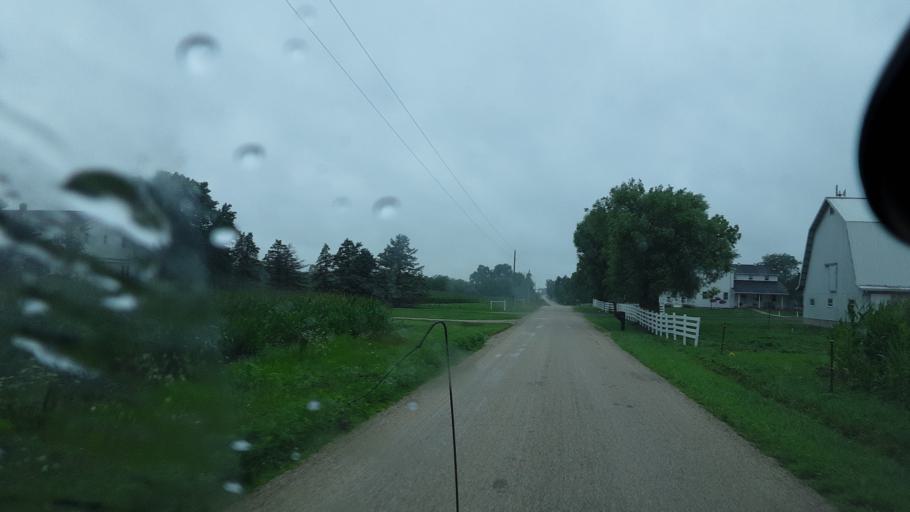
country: US
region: Indiana
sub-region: Adams County
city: Berne
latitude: 40.7035
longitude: -84.8274
